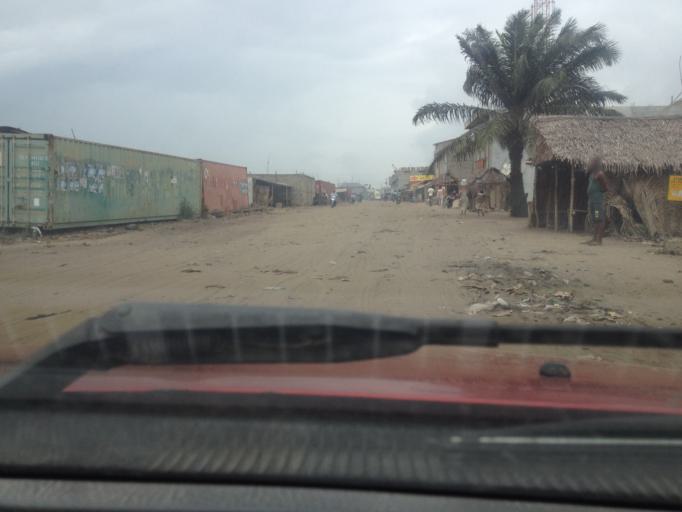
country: BJ
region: Queme
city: Porto-Novo
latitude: 6.3831
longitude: 2.7051
